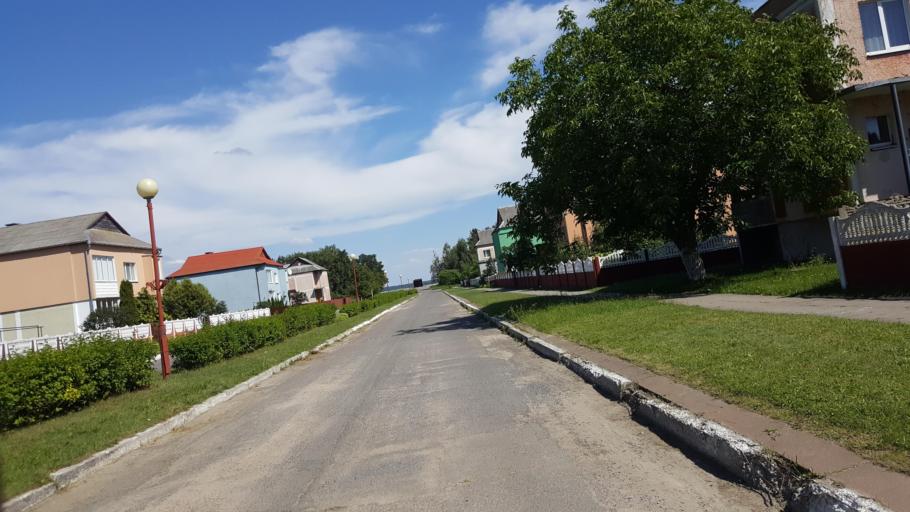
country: BY
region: Brest
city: Charnawchytsy
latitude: 52.2665
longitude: 23.5931
